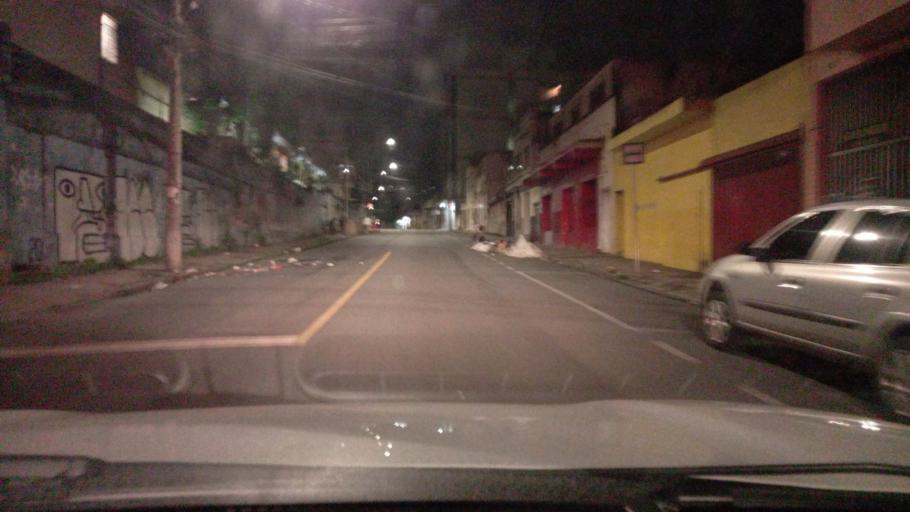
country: BR
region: Minas Gerais
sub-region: Belo Horizonte
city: Belo Horizonte
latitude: -19.9082
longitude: -43.9447
